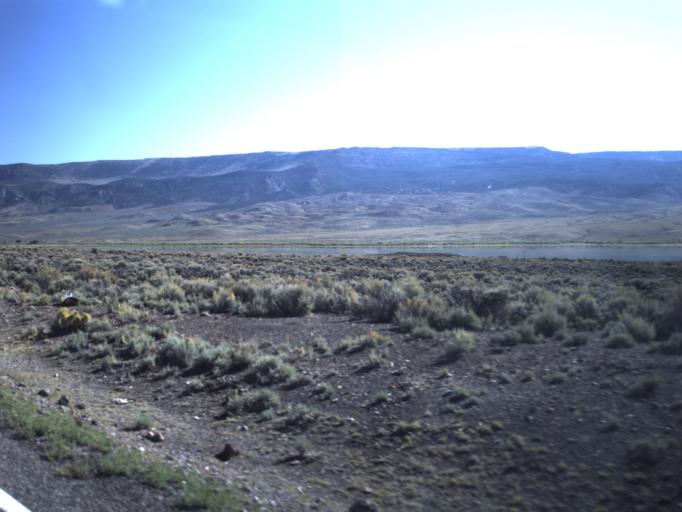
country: US
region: Utah
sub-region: Piute County
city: Junction
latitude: 38.1801
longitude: -112.0194
